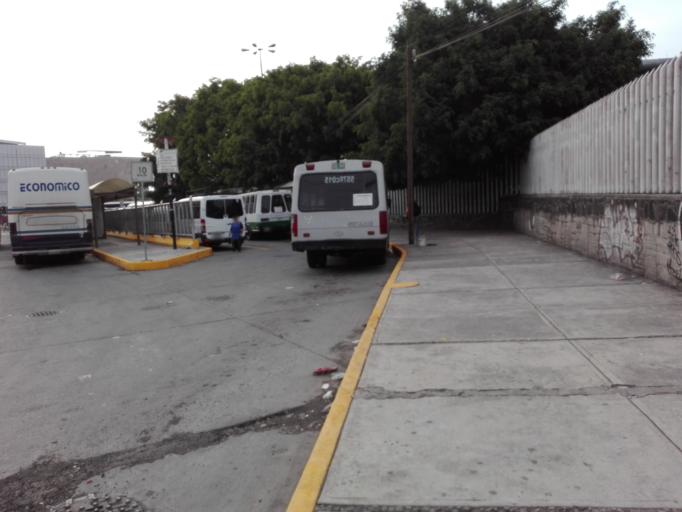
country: MX
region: Mexico City
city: Mexico City
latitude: 19.4294
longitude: -99.1141
